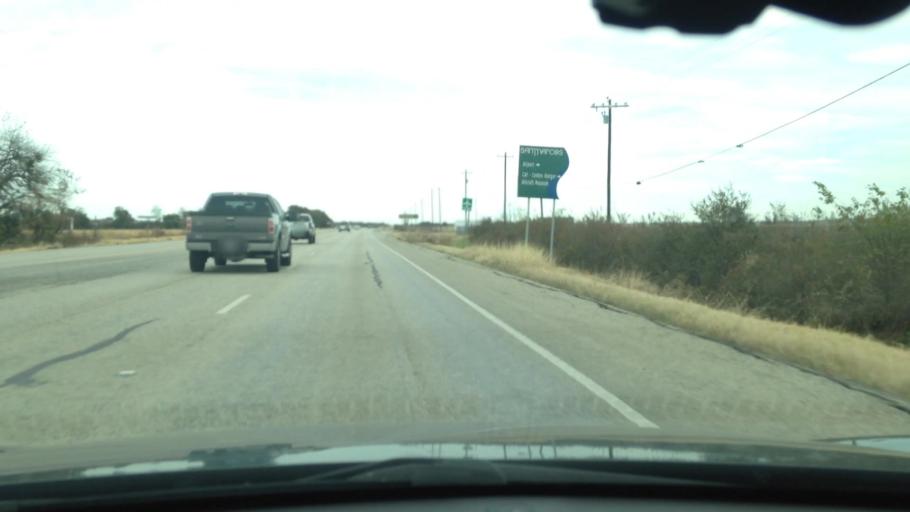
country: US
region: Texas
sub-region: Hays County
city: San Marcos
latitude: 29.8932
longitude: -97.8812
